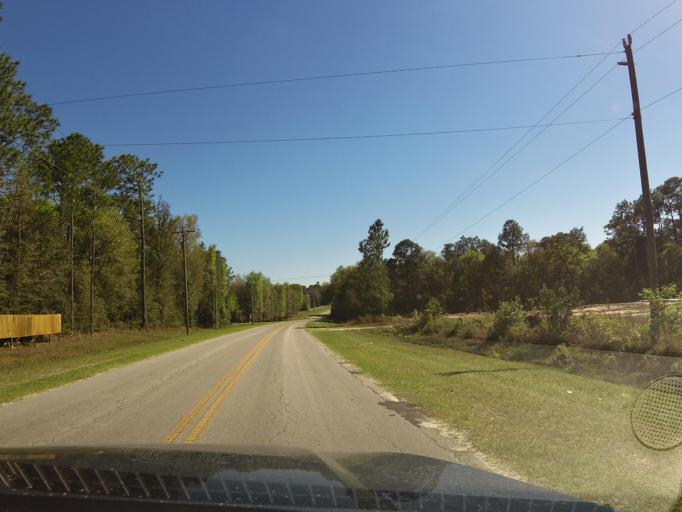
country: US
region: Florida
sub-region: Clay County
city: Keystone Heights
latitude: 29.8215
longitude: -82.0583
